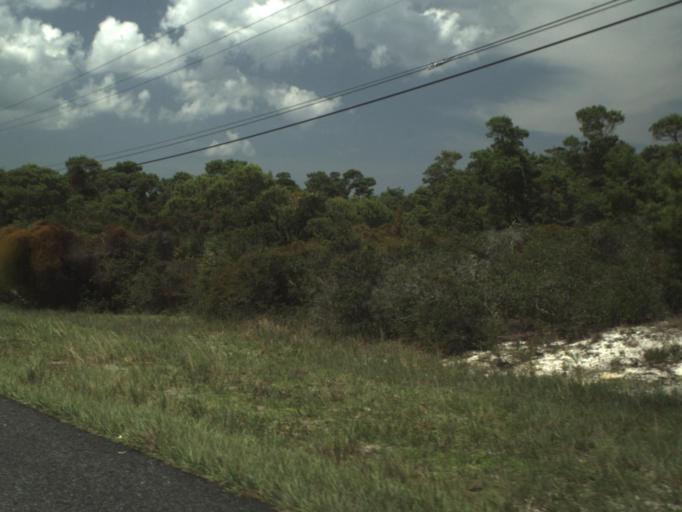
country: US
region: Florida
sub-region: Martin County
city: Hobe Sound
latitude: 27.0256
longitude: -80.1090
